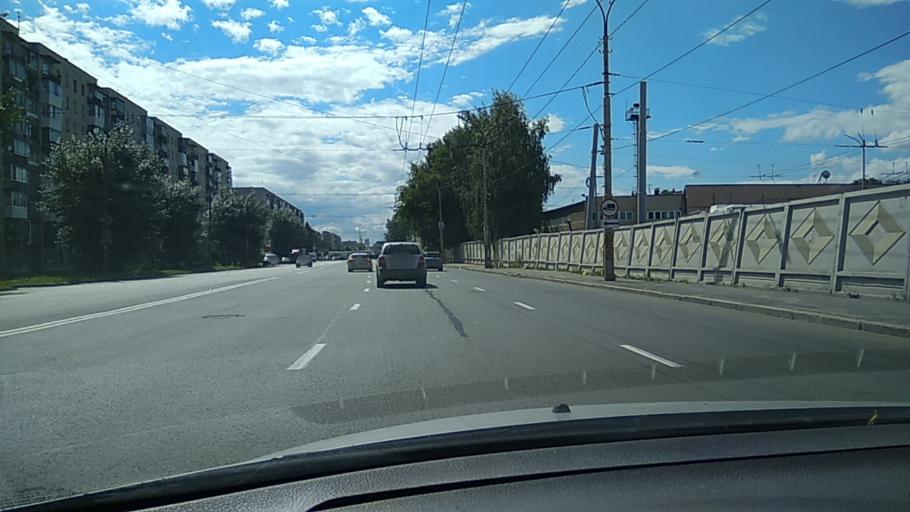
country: RU
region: Sverdlovsk
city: Verkhnyaya Pyshma
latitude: 56.9111
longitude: 60.5949
